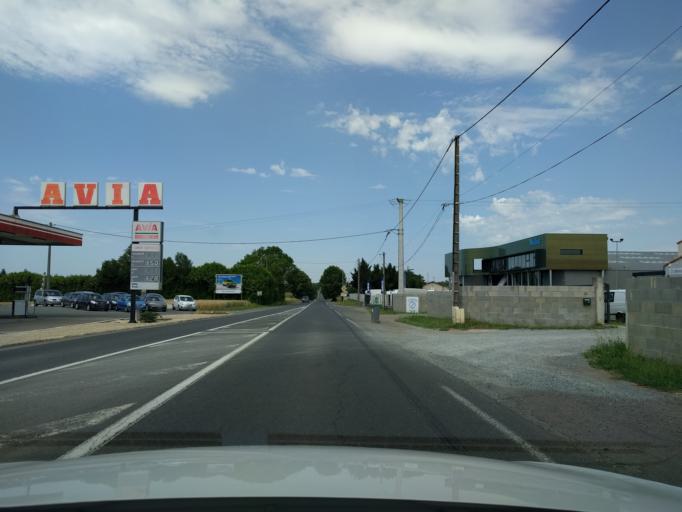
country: FR
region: Poitou-Charentes
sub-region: Departement des Deux-Sevres
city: Niort
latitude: 46.3418
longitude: -0.4916
